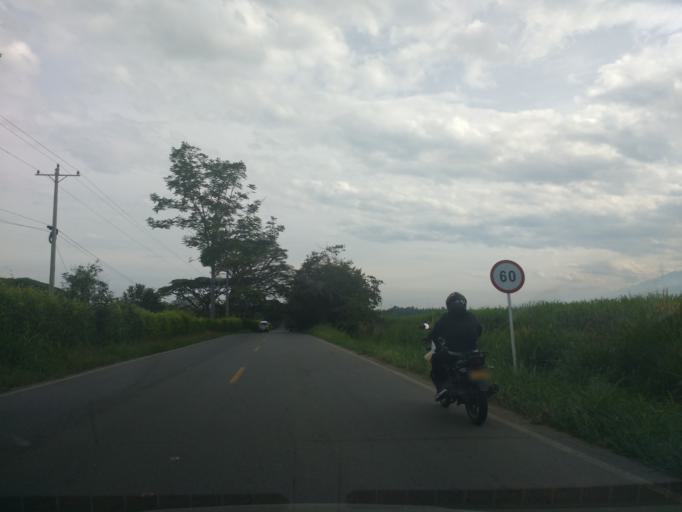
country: CO
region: Valle del Cauca
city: Florida
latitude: 3.3026
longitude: -76.2323
